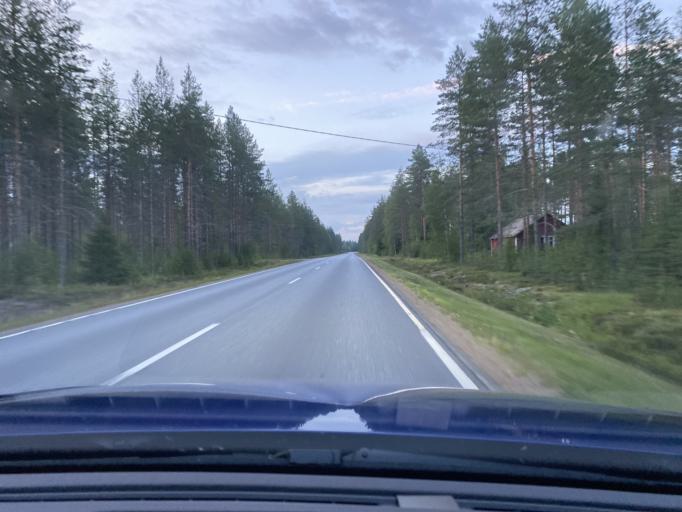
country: FI
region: Satakunta
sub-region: Pohjois-Satakunta
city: Honkajoki
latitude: 62.1383
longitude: 22.2540
